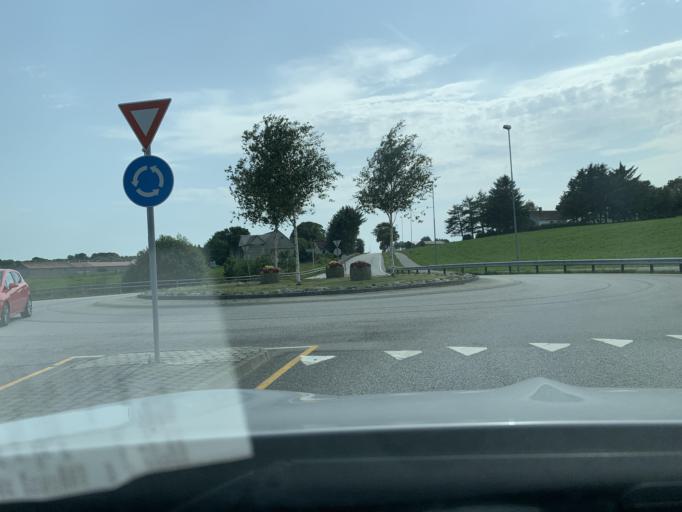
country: NO
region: Rogaland
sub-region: Klepp
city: Kleppe
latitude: 58.7675
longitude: 5.6286
